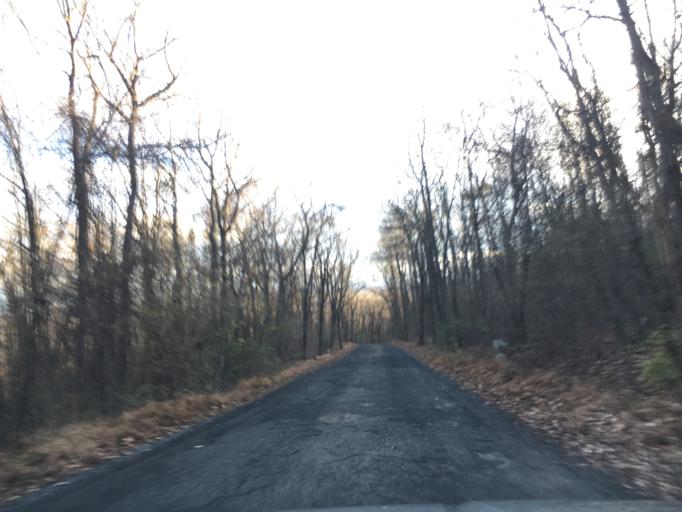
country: US
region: Pennsylvania
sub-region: Carbon County
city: Lehighton
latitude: 40.7659
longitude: -75.6956
